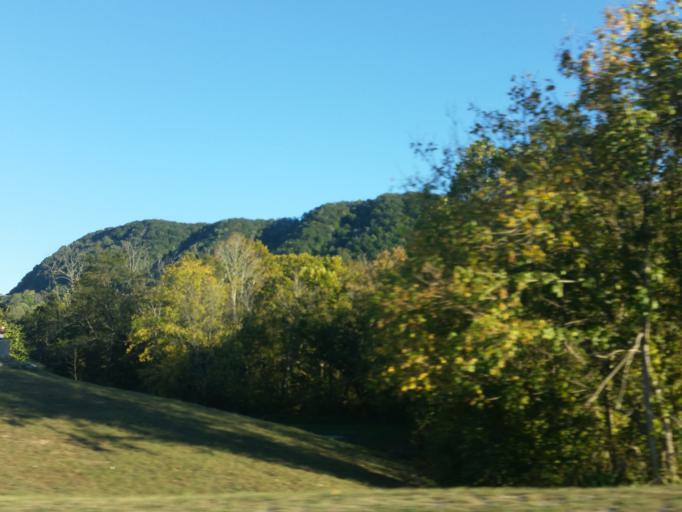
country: US
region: Tennessee
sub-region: Grainger County
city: Rutledge
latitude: 36.3589
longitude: -83.4161
